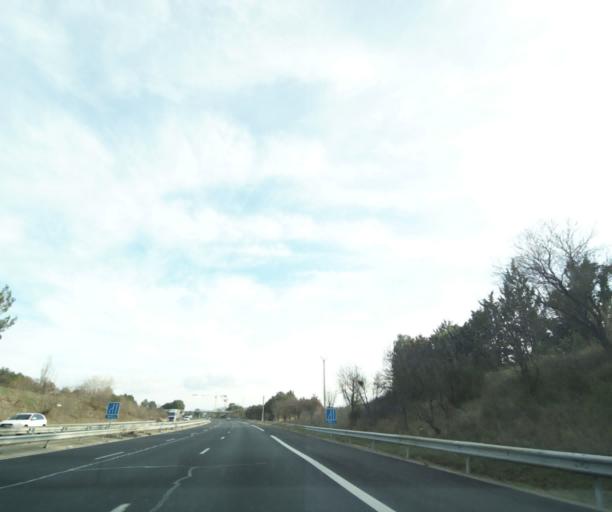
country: FR
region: Provence-Alpes-Cote d'Azur
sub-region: Departement des Bouches-du-Rhone
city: Aix-en-Provence
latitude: 43.5212
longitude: 5.4138
